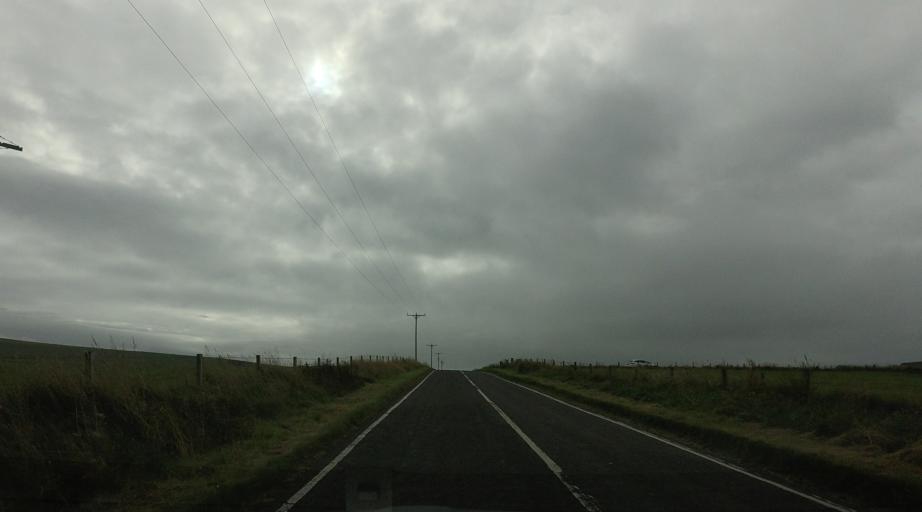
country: GB
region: Scotland
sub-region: Orkney Islands
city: Orkney
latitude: 58.7875
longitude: -2.9588
